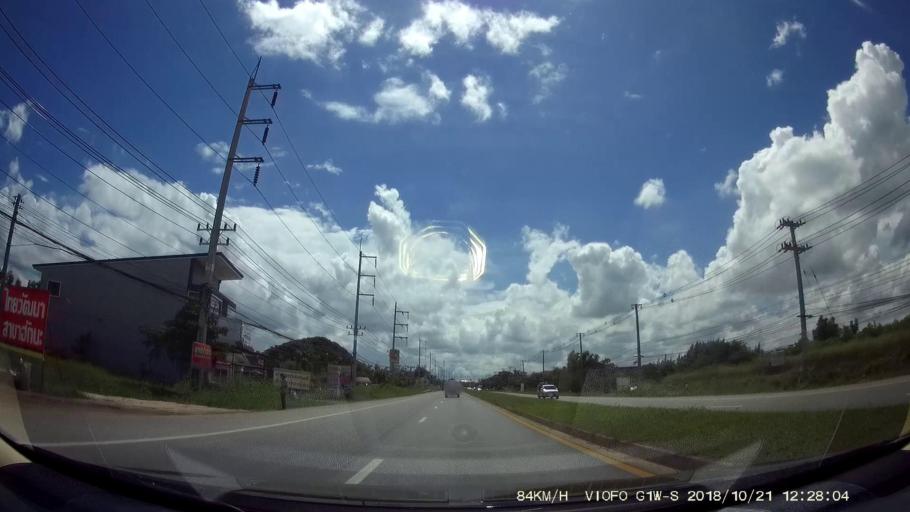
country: TH
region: Nakhon Ratchasima
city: Dan Khun Thot
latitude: 15.1939
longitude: 101.7617
